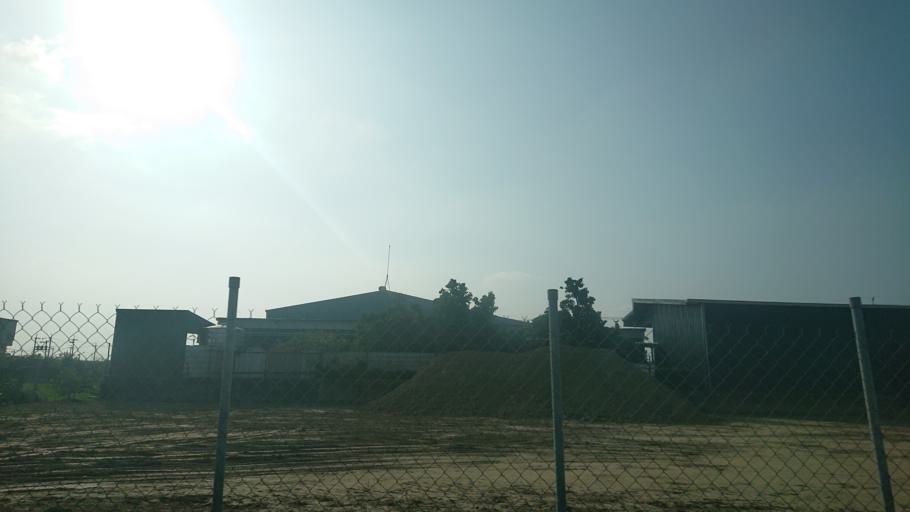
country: TW
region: Taiwan
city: Xinying
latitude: 23.2028
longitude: 120.2711
